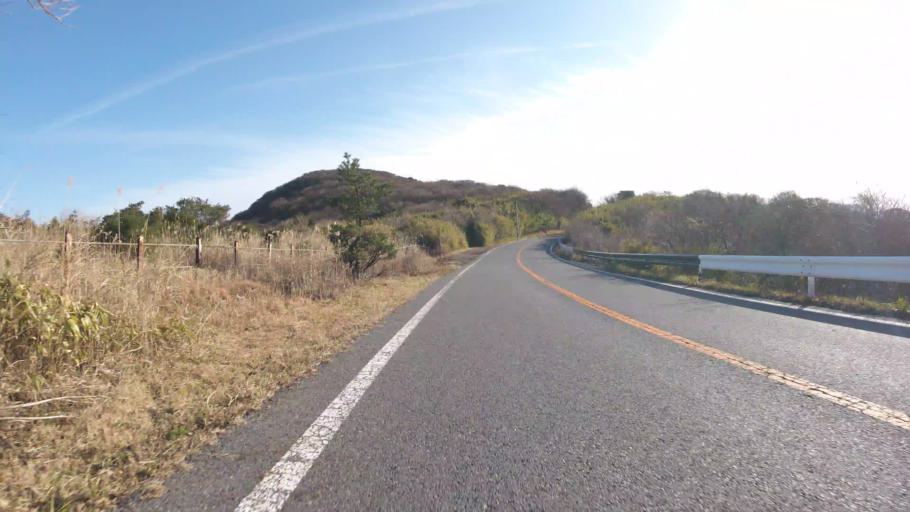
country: JP
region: Kanagawa
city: Hakone
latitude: 35.1583
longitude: 139.0257
